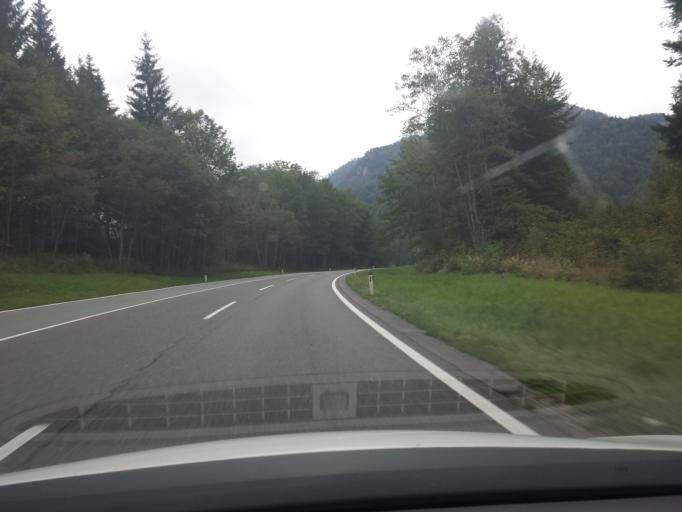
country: AT
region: Salzburg
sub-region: Politischer Bezirk Salzburg-Umgebung
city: Sankt Gilgen
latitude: 47.7766
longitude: 13.3479
